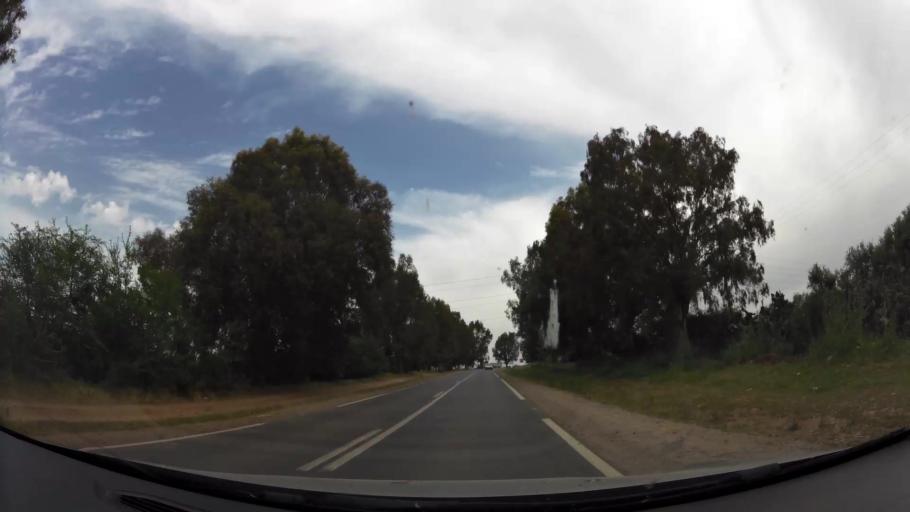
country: MA
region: Rabat-Sale-Zemmour-Zaer
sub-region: Khemisset
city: Tiflet
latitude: 33.8544
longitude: -6.2687
